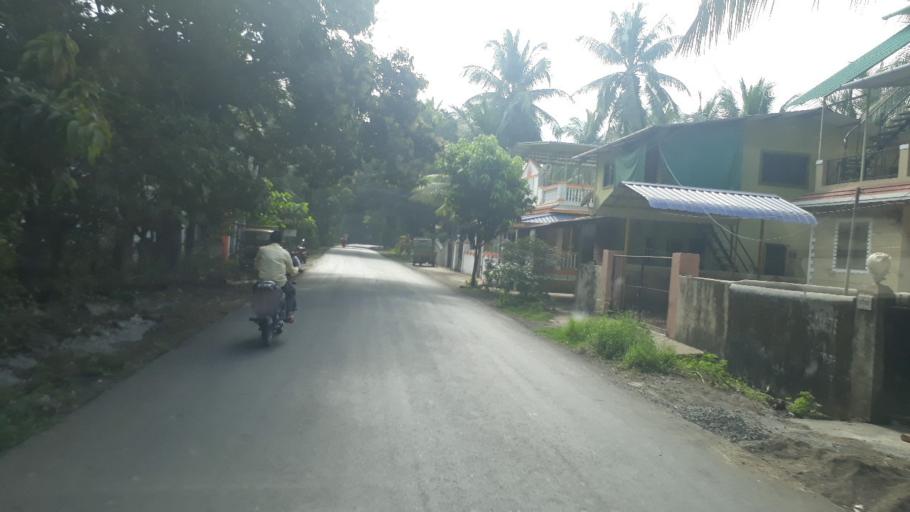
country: IN
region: Maharashtra
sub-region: Raigarh
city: Revadanda
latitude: 18.5899
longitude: 72.9253
